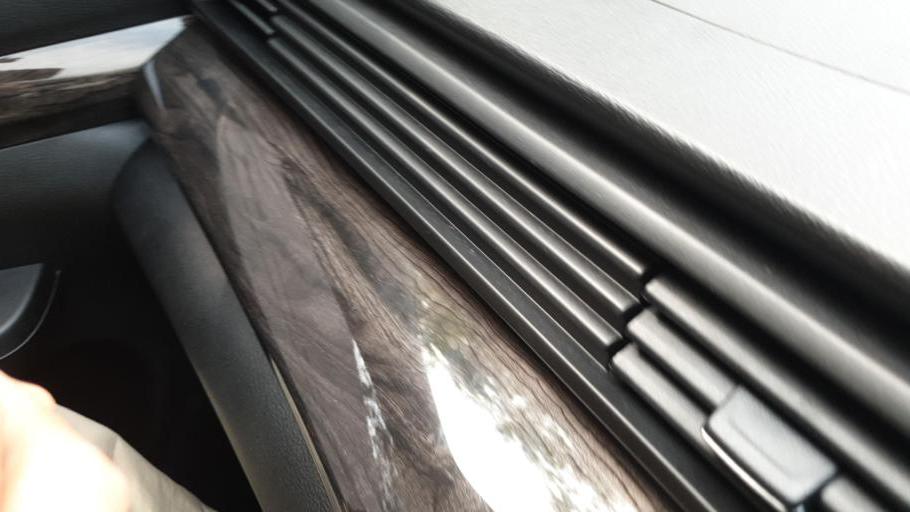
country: ID
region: Jakarta Raya
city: Jakarta
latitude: -6.2491
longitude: 106.7813
